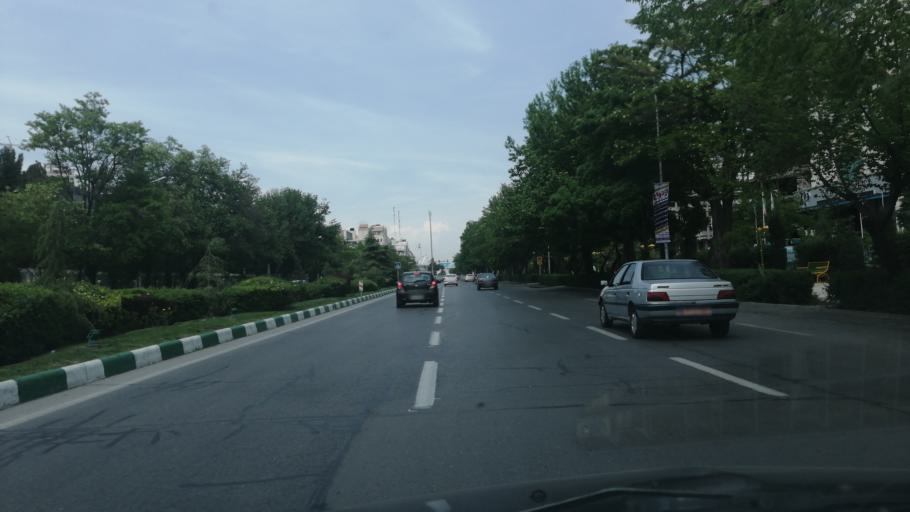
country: IR
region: Razavi Khorasan
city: Mashhad
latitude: 36.3178
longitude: 59.5635
